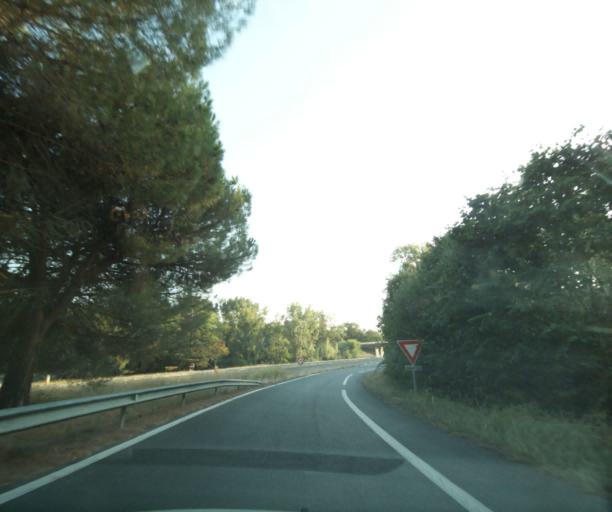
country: FR
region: Midi-Pyrenees
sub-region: Departement du Tarn-et-Garonne
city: Castelsarrasin
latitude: 44.0531
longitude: 1.0953
